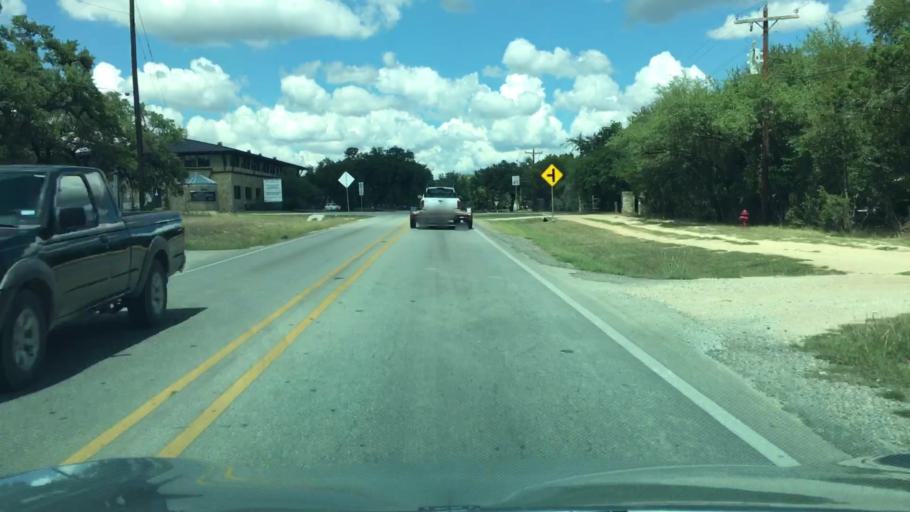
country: US
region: Texas
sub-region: Hays County
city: Wimberley
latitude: 29.9961
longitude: -98.0905
